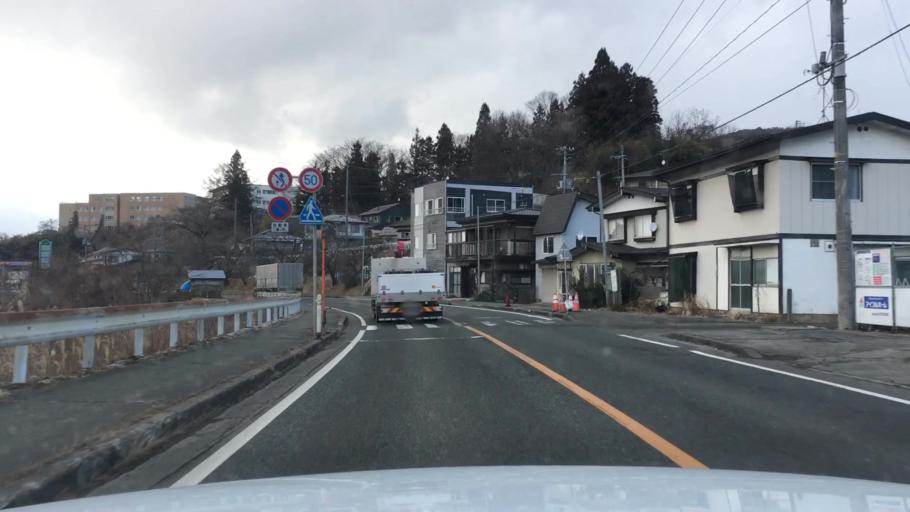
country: JP
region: Iwate
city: Morioka-shi
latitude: 39.6860
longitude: 141.1817
